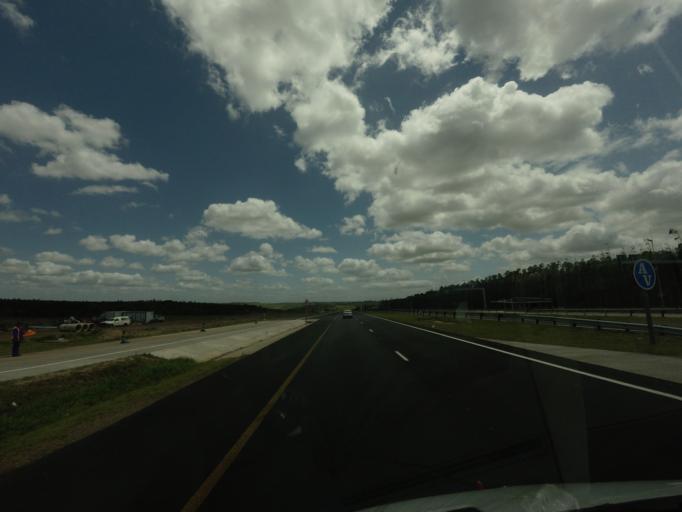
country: ZA
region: KwaZulu-Natal
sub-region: uThungulu District Municipality
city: KwaMbonambi
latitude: -28.5144
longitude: 32.1377
